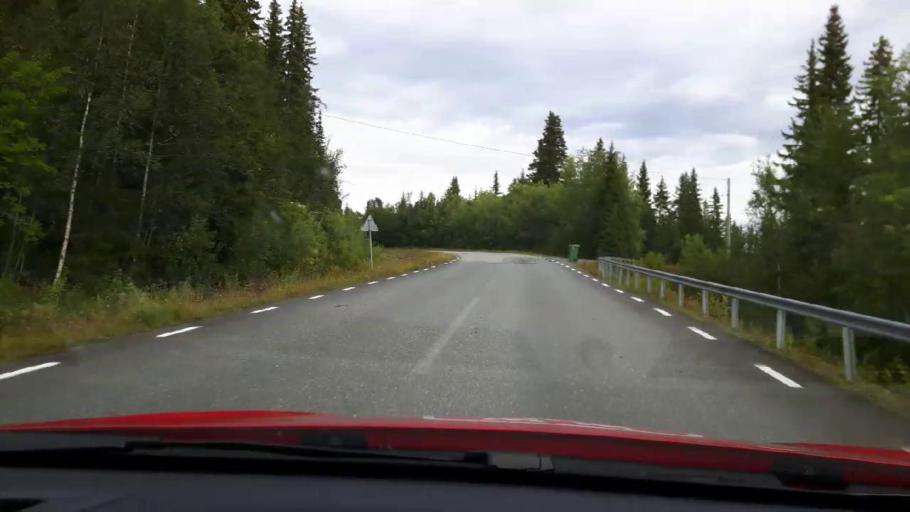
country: SE
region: Jaemtland
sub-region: Are Kommun
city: Are
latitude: 63.7030
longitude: 12.9495
